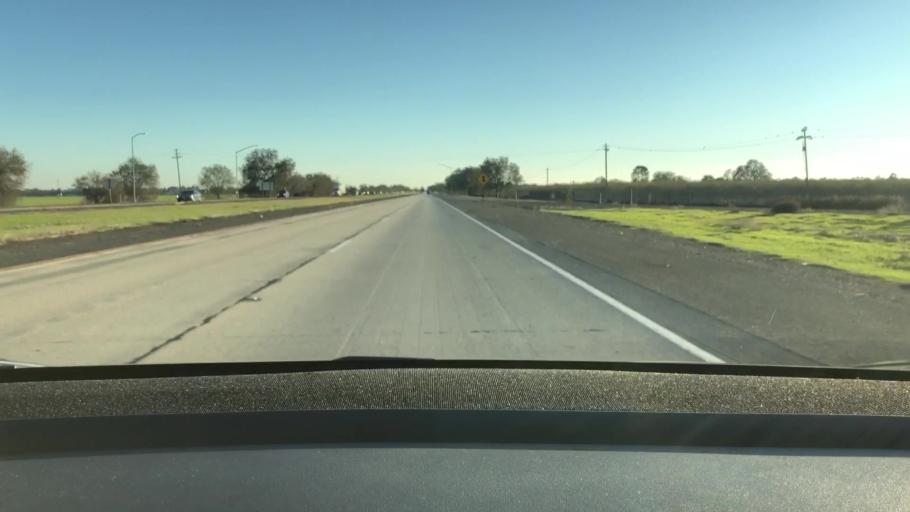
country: US
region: California
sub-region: Yolo County
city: Woodland
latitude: 38.6171
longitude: -121.7670
